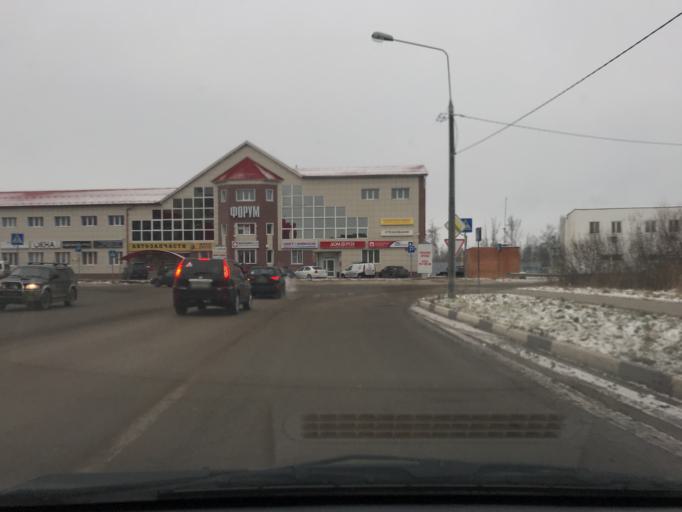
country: RU
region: Moskovskaya
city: Elektrostal'
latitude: 55.8134
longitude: 38.4320
